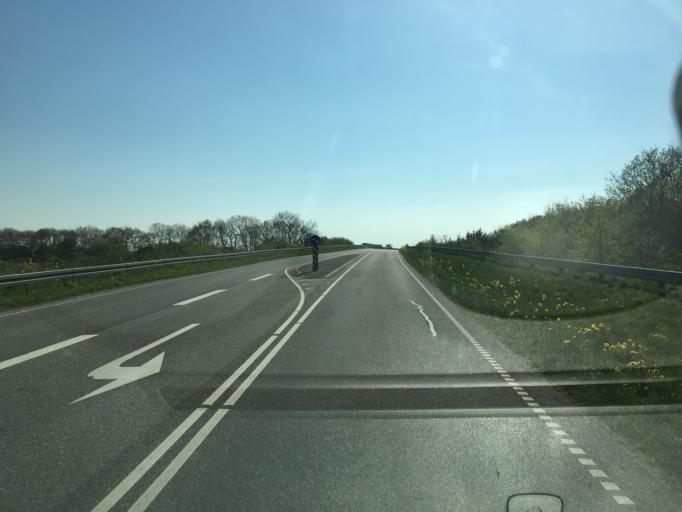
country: DK
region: South Denmark
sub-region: Haderslev Kommune
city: Vojens
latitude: 55.3120
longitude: 9.2899
